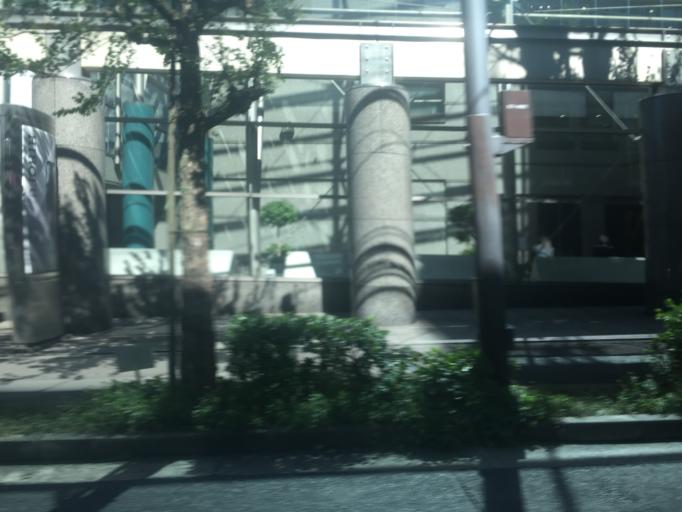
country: JP
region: Tokyo
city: Tokyo
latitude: 35.6447
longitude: 139.7091
